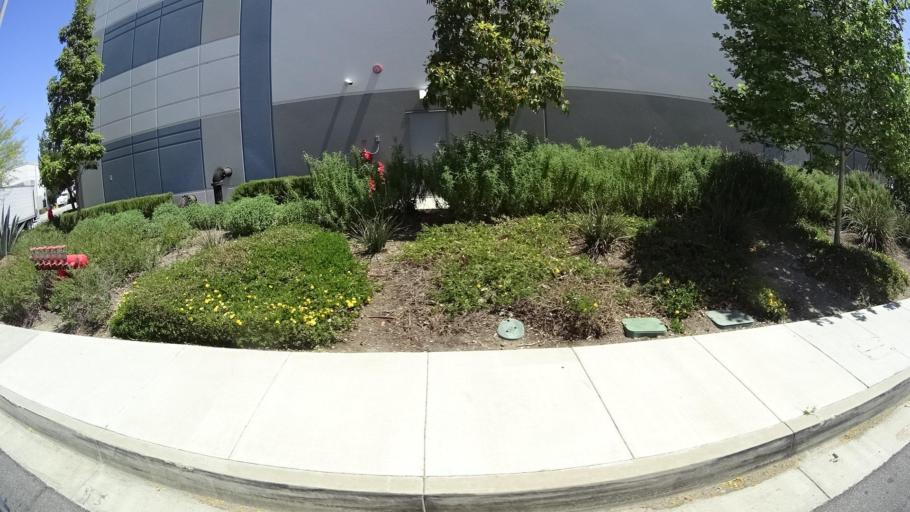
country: US
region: California
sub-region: Los Angeles County
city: La Puente
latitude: 34.0184
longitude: -117.9620
